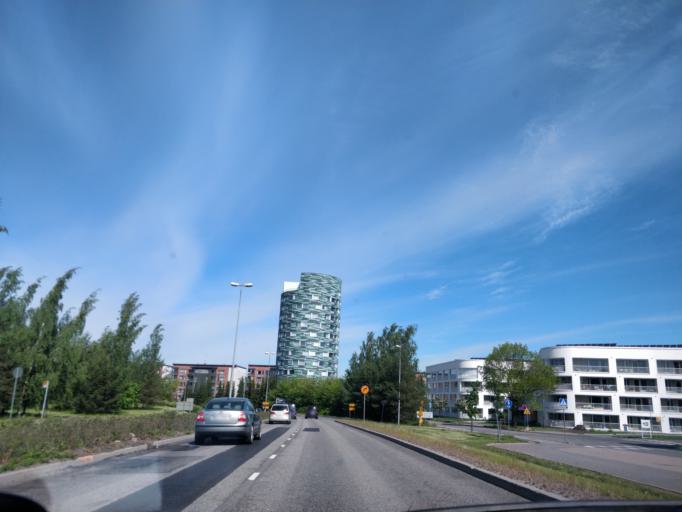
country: FI
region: Varsinais-Suomi
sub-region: Turku
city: Turku
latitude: 60.4593
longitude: 22.2882
